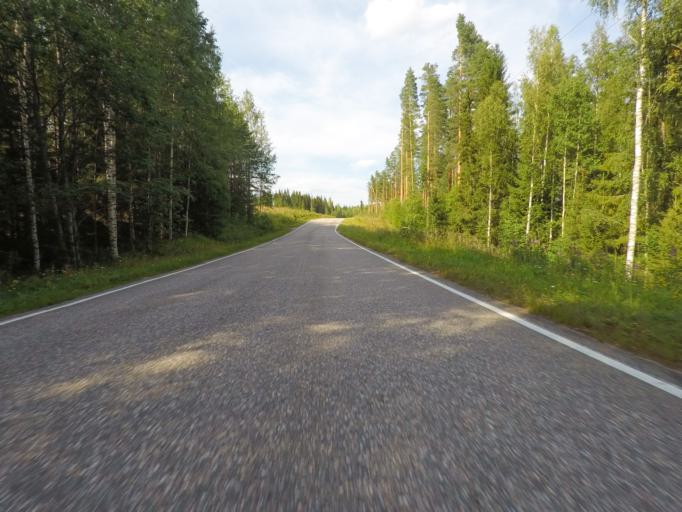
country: FI
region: Southern Savonia
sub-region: Savonlinna
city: Sulkava
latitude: 61.7746
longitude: 28.2391
